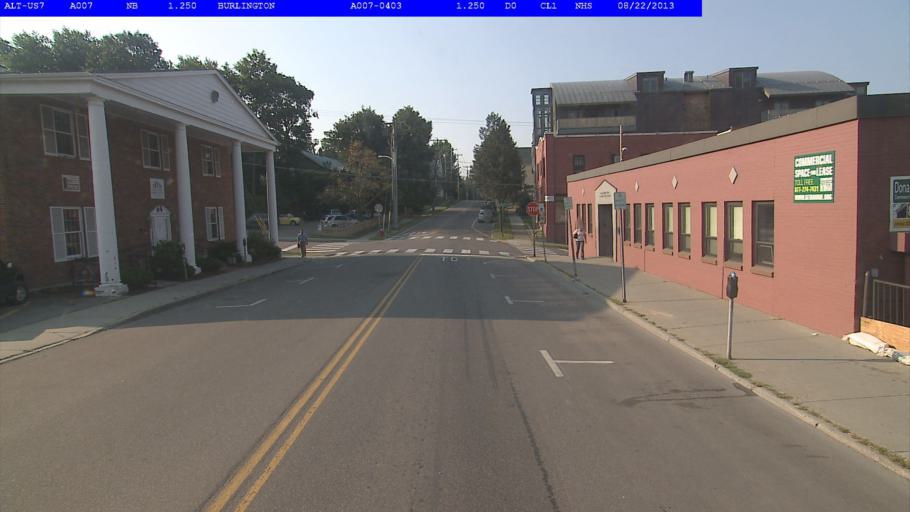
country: US
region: Vermont
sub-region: Chittenden County
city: Burlington
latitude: 44.4752
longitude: -73.2109
